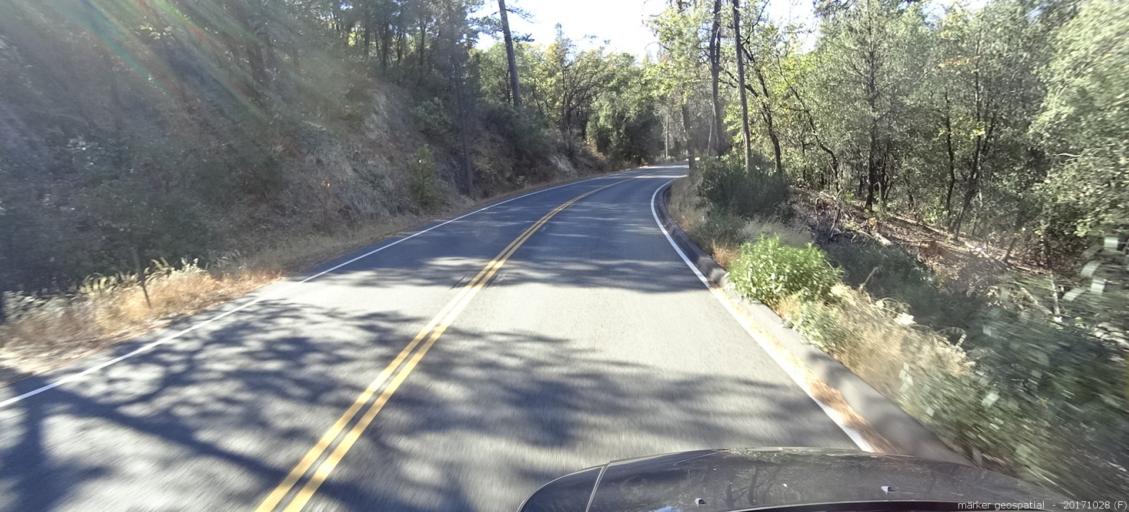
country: US
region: California
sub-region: Shasta County
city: Shasta
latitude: 40.6037
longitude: -122.5328
